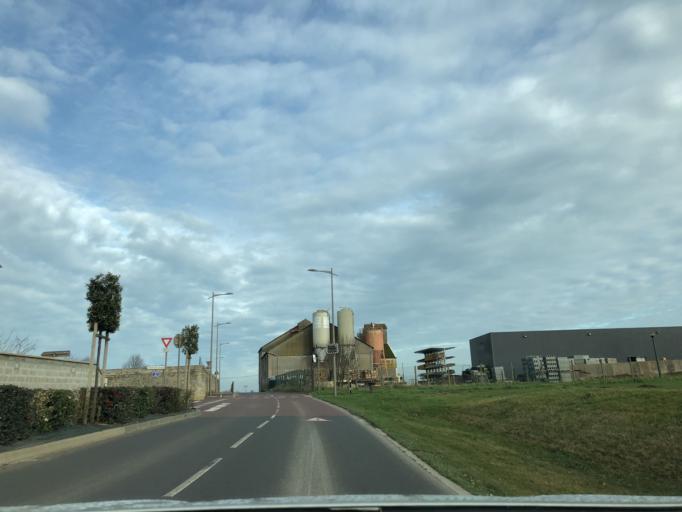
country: FR
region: Lower Normandy
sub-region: Departement du Calvados
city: Douvres-la-Delivrande
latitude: 49.2933
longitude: -0.3675
